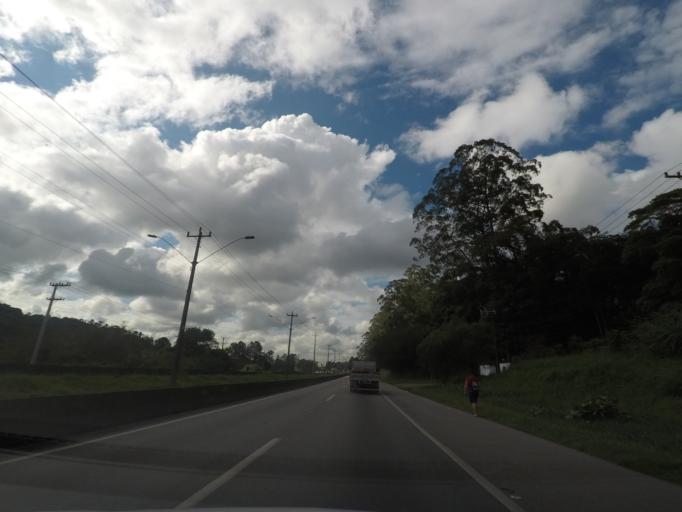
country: BR
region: Sao Paulo
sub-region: Itapecerica Da Serra
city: Itapecerica da Serra
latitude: -23.6979
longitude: -46.8660
